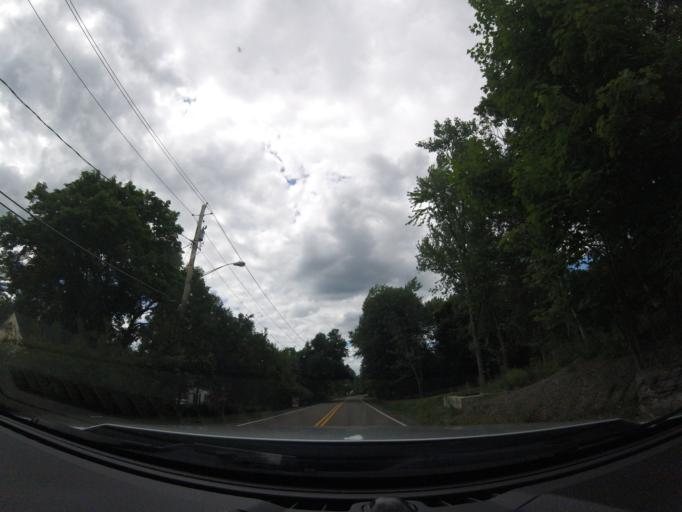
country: US
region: New York
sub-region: Tompkins County
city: Cayuga Heights
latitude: 42.4733
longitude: -76.4971
